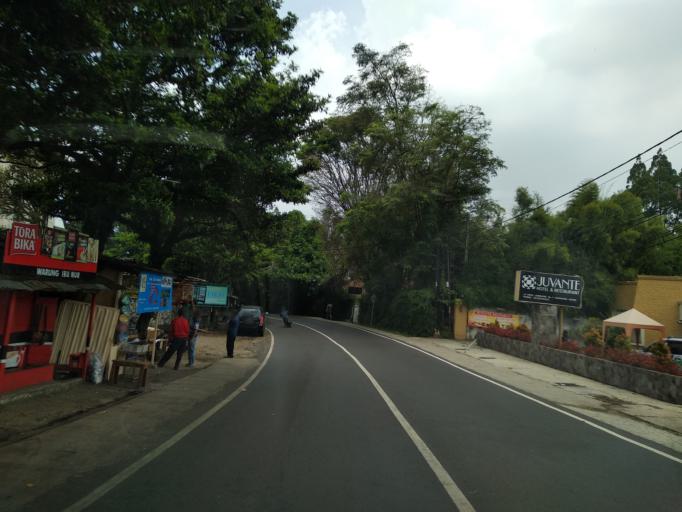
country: ID
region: West Java
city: Lembang
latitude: -6.8400
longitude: 107.5973
